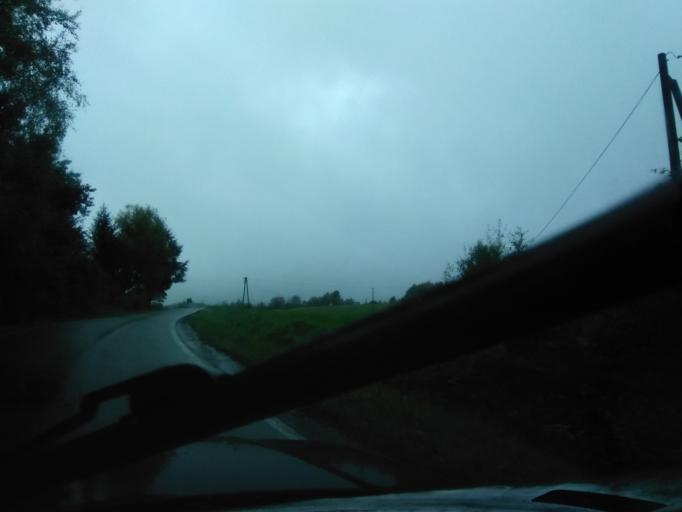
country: PL
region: Subcarpathian Voivodeship
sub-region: Powiat ropczycko-sedziszowski
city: Niedzwiada
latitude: 50.0424
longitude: 21.5433
